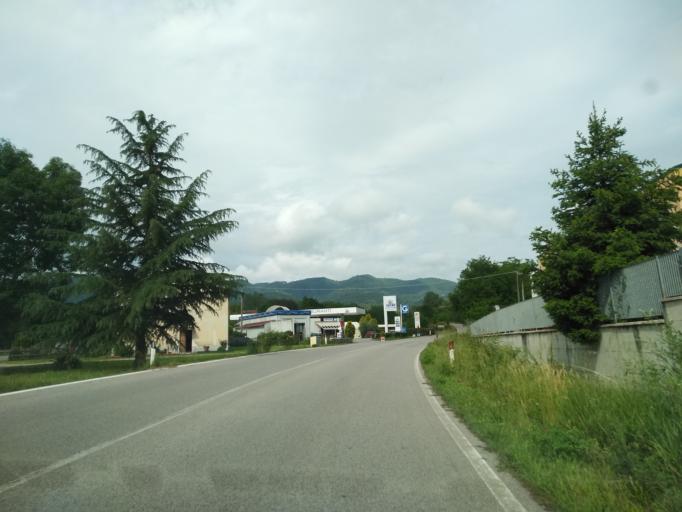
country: IT
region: Tuscany
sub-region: Province of Arezzo
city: San Cipriano-S.Barbara-Centinale
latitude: 43.5613
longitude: 11.4657
